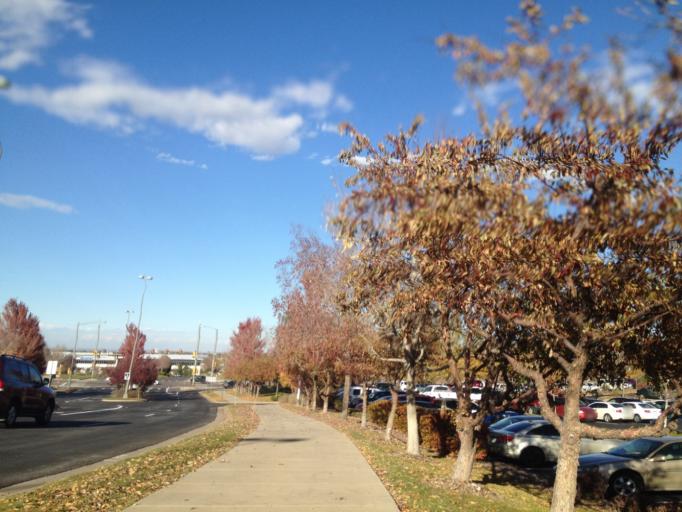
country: US
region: Colorado
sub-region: Broomfield County
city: Broomfield
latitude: 39.9145
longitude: -105.1064
